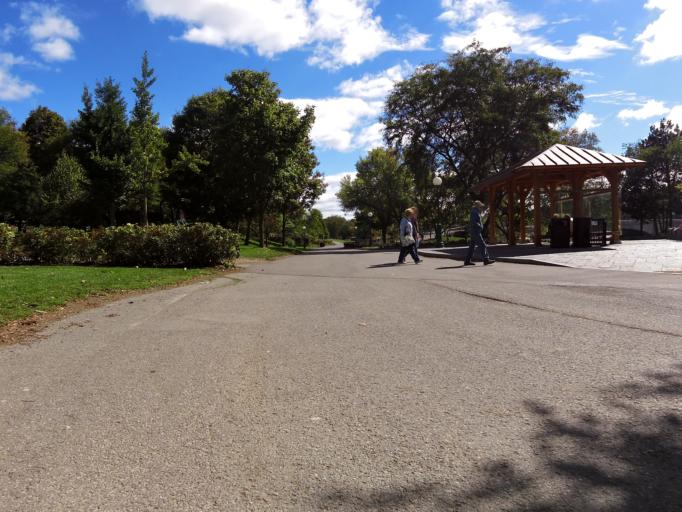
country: US
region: New York
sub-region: Niagara County
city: Niagara Falls
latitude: 43.0856
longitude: -79.0662
